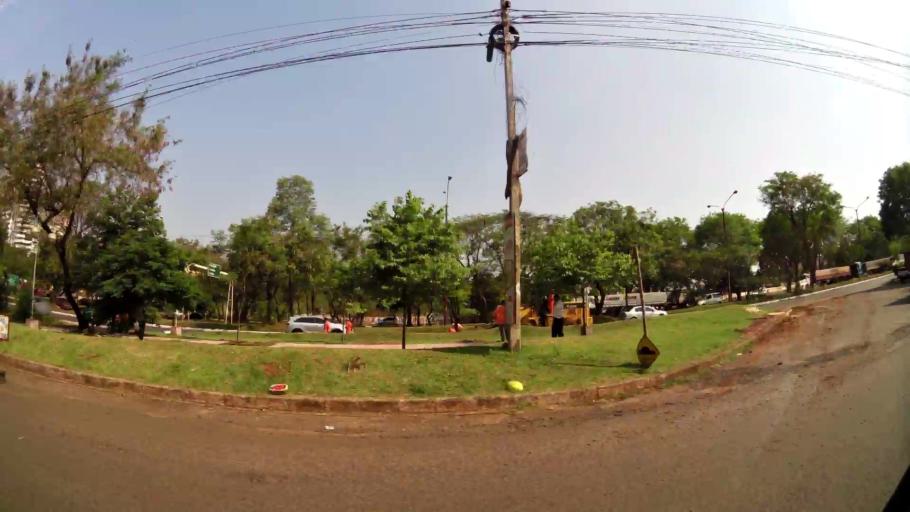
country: PY
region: Alto Parana
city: Ciudad del Este
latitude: -25.5092
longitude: -54.6178
